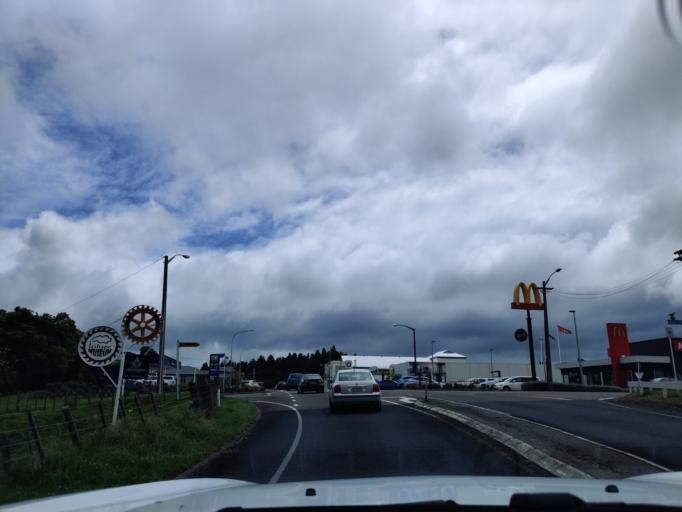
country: NZ
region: Manawatu-Wanganui
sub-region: Ruapehu District
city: Waiouru
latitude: -39.6801
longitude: 175.8004
